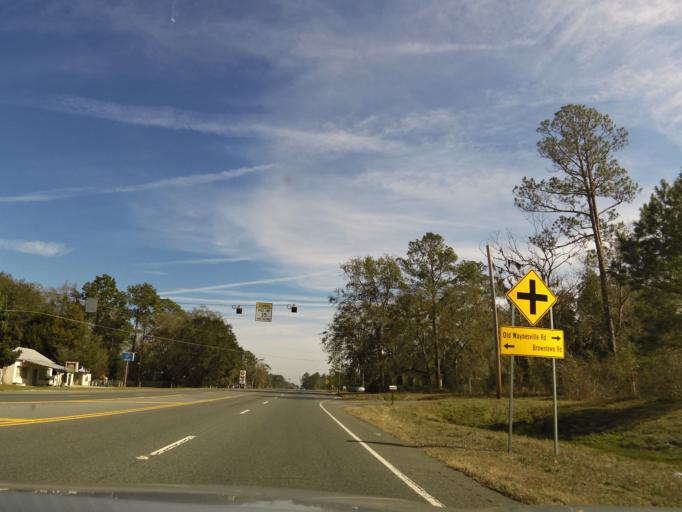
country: US
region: Georgia
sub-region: Brantley County
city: Nahunta
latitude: 31.2289
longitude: -81.7934
